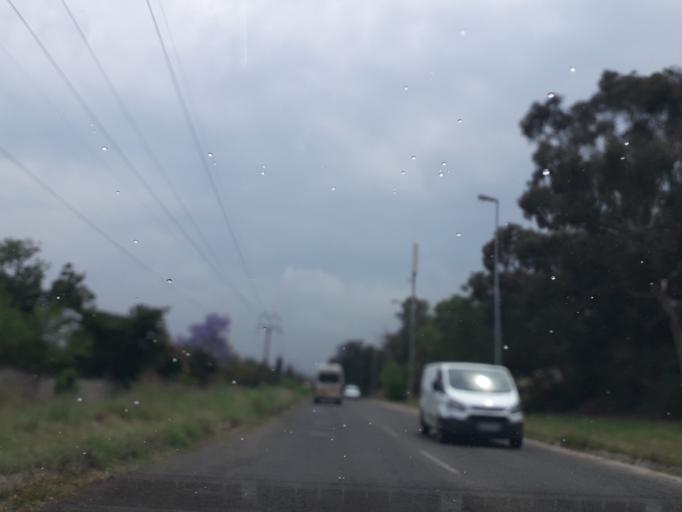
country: ZA
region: Gauteng
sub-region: City of Johannesburg Metropolitan Municipality
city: Roodepoort
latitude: -26.0782
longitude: 27.9567
